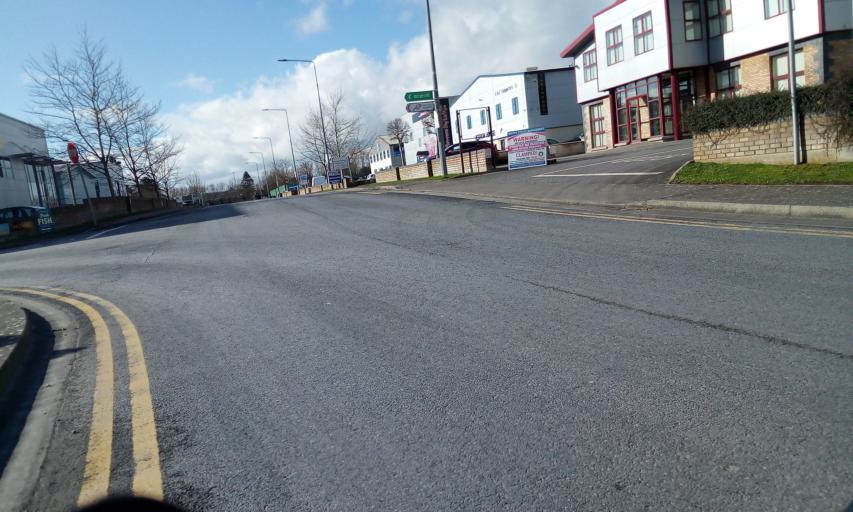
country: IE
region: Leinster
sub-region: Kilkenny
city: Kilkenny
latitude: 52.6539
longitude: -7.2320
